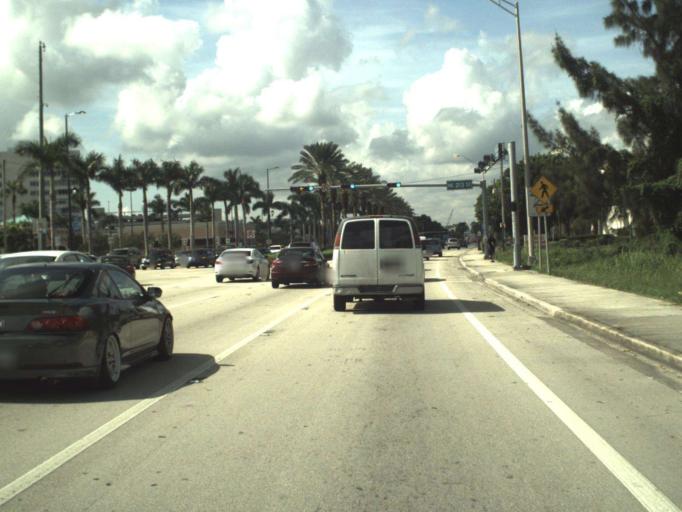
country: US
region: Florida
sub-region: Broward County
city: Hallandale Beach
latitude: 25.9736
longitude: -80.1427
